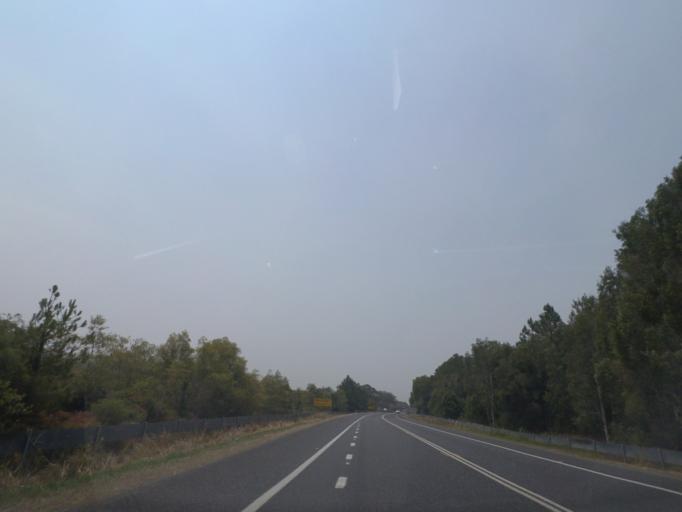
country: AU
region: New South Wales
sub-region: Ballina
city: Ballina
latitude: -28.9374
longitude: 153.4707
